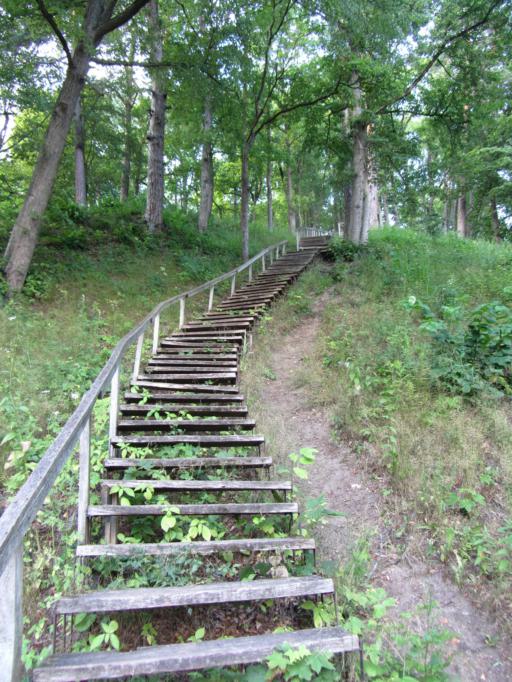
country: LT
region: Vilnius County
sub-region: Vilnius
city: Fabijoniskes
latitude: 54.7459
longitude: 25.2913
